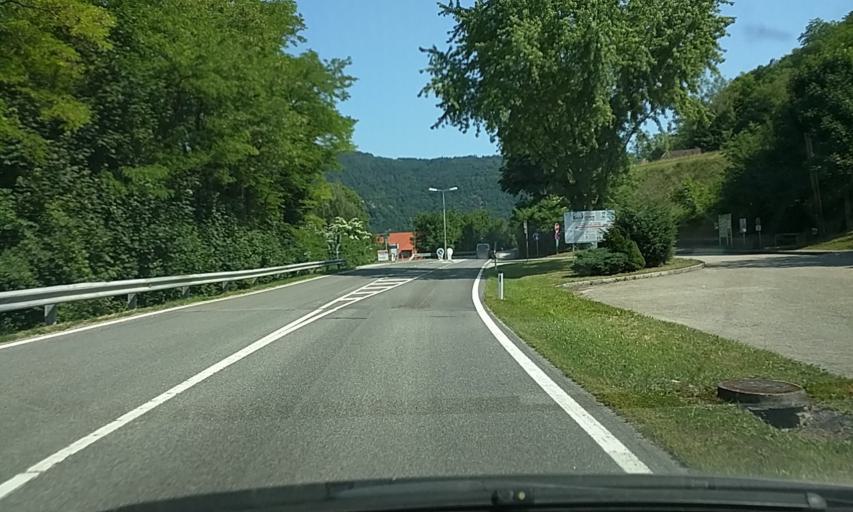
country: AT
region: Lower Austria
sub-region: Politischer Bezirk Krems
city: Aggsbach
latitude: 48.2621
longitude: 15.3780
